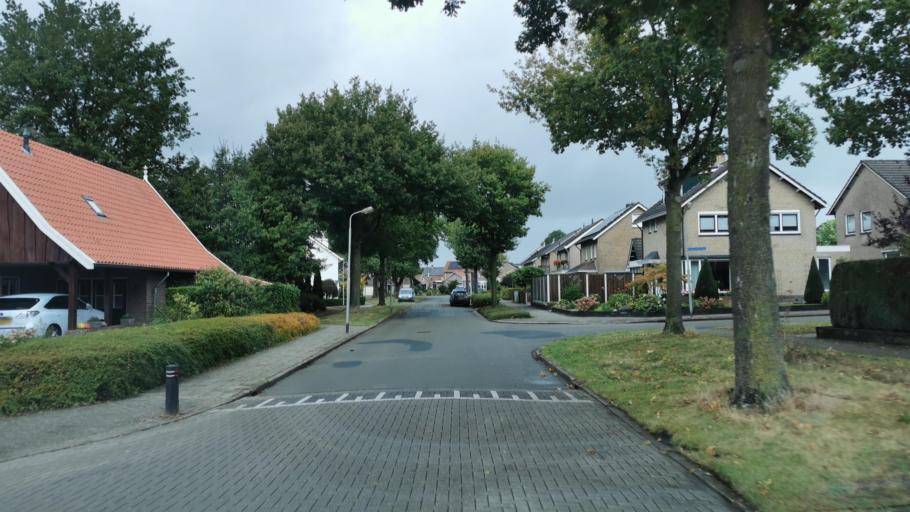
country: NL
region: Overijssel
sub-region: Gemeente Losser
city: Losser
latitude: 52.3120
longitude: 6.9913
